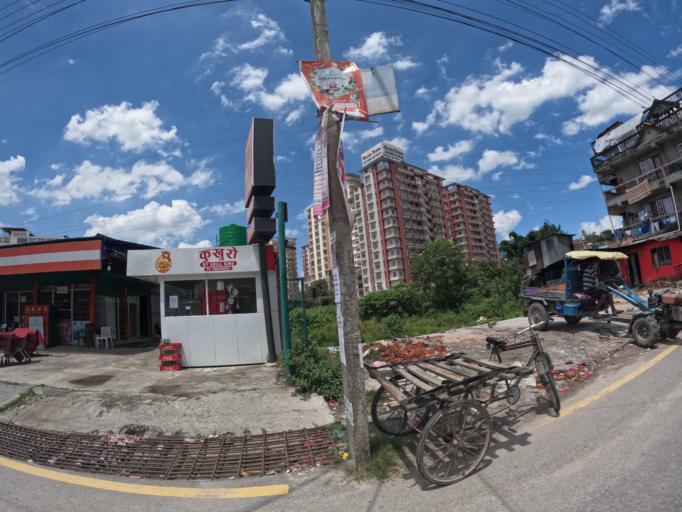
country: NP
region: Central Region
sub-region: Bagmati Zone
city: Kathmandu
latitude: 27.7537
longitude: 85.3275
